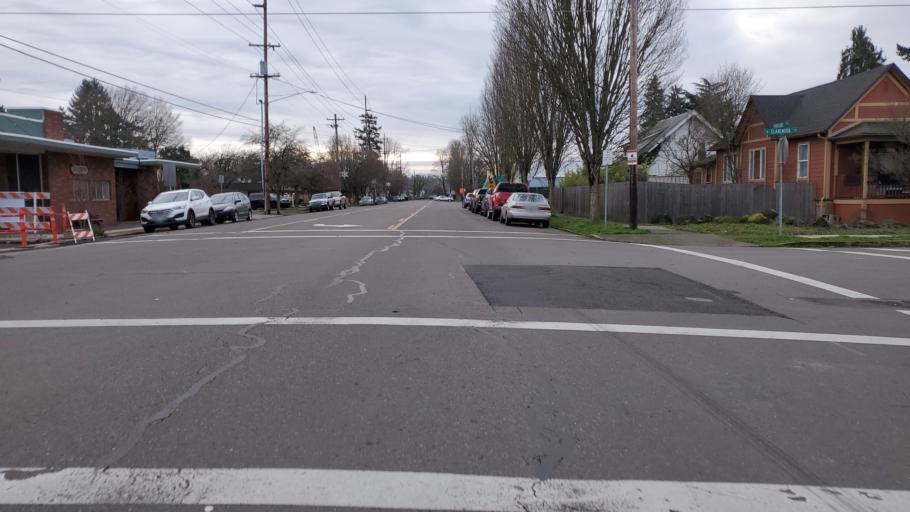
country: US
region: Oregon
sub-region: Clackamas County
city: Gladstone
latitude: 45.3797
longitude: -122.5943
